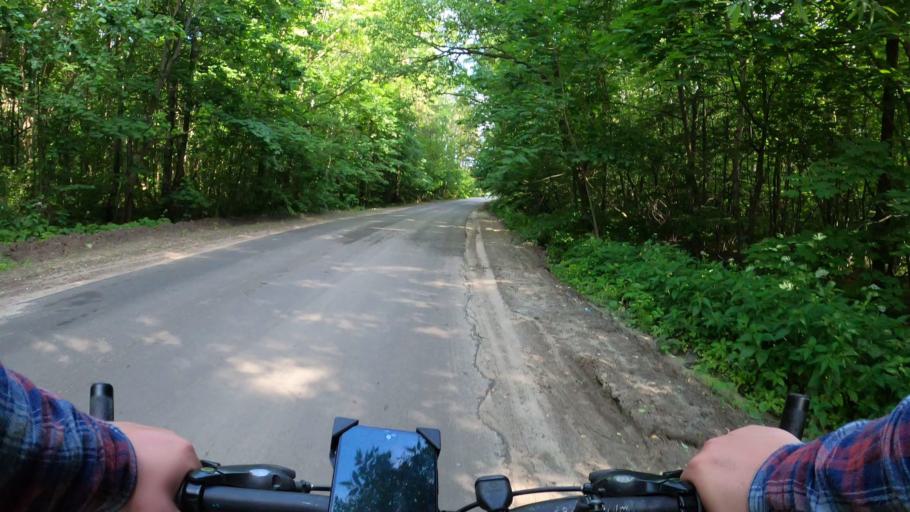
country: RU
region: Moskovskaya
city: Ashitkovo
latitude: 55.4387
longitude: 38.6324
